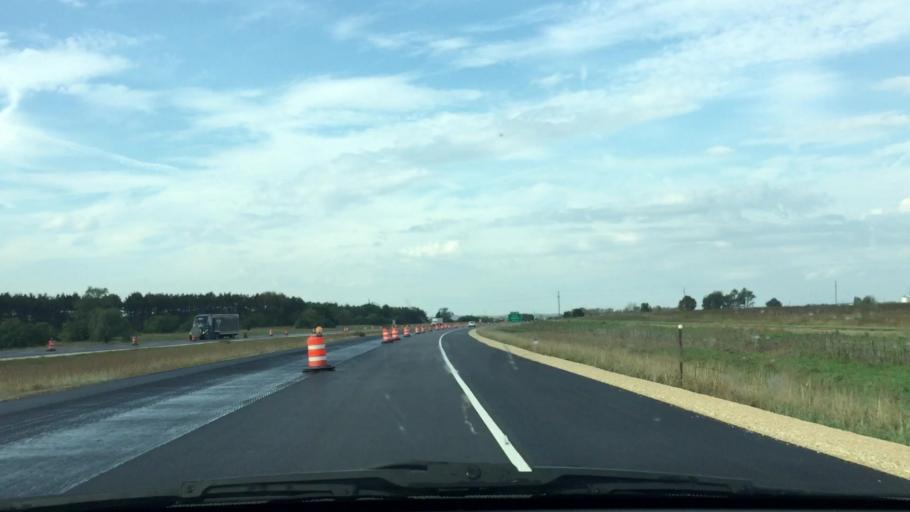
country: US
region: Illinois
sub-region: Whiteside County
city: Erie
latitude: 41.6910
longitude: -90.0789
